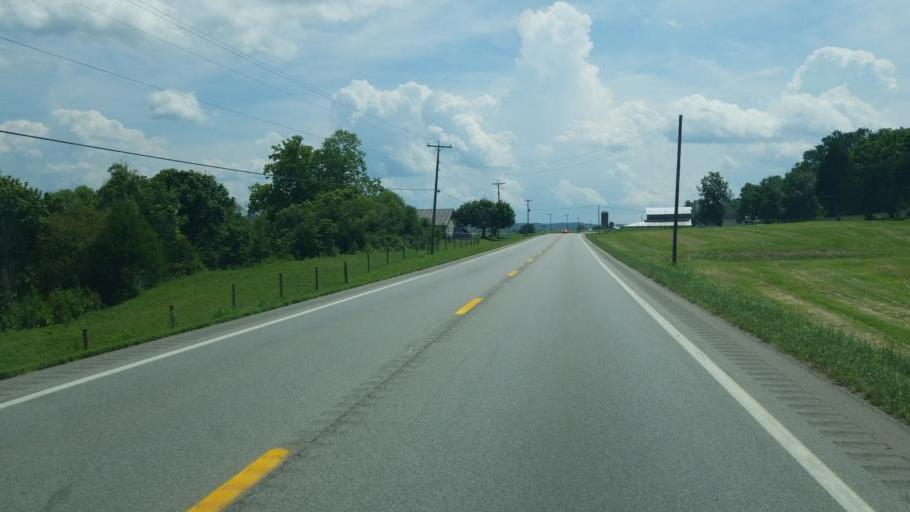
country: US
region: West Virginia
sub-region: Putnam County
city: Buffalo
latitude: 38.7412
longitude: -81.9782
